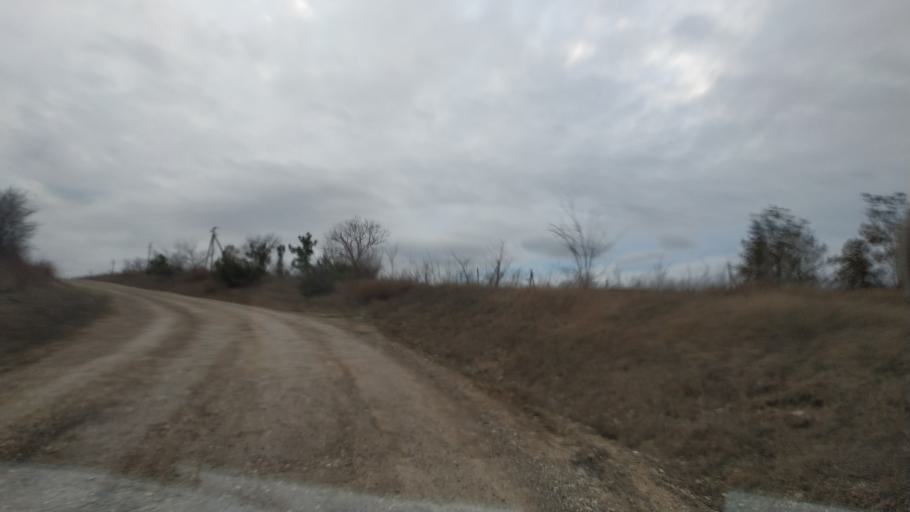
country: MD
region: Causeni
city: Causeni
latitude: 46.6263
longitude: 29.3969
